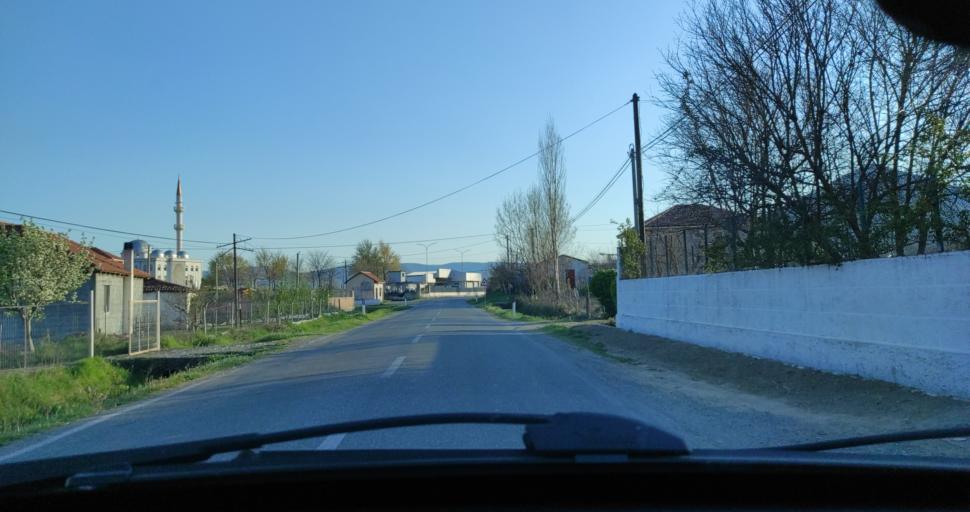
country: AL
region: Shkoder
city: Vukatane
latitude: 41.9733
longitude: 19.5426
